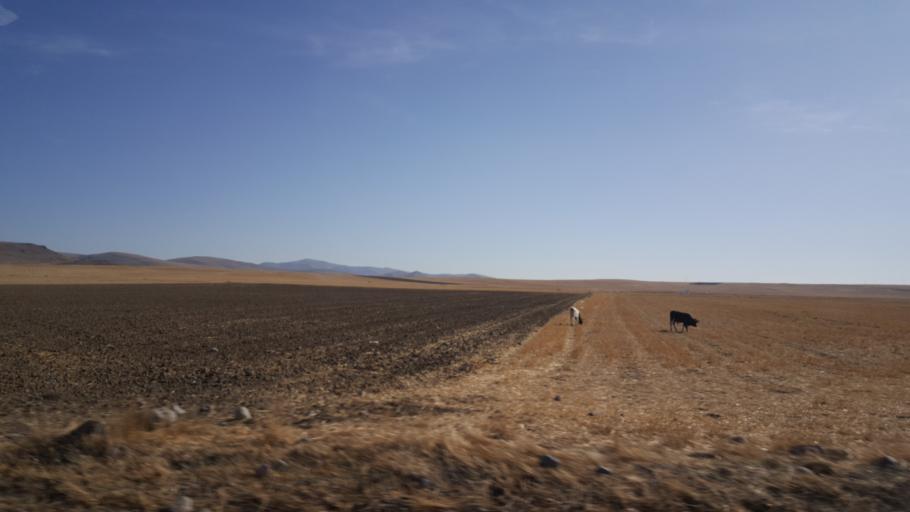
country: TR
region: Ankara
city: Yenice
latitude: 39.3458
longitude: 32.7590
